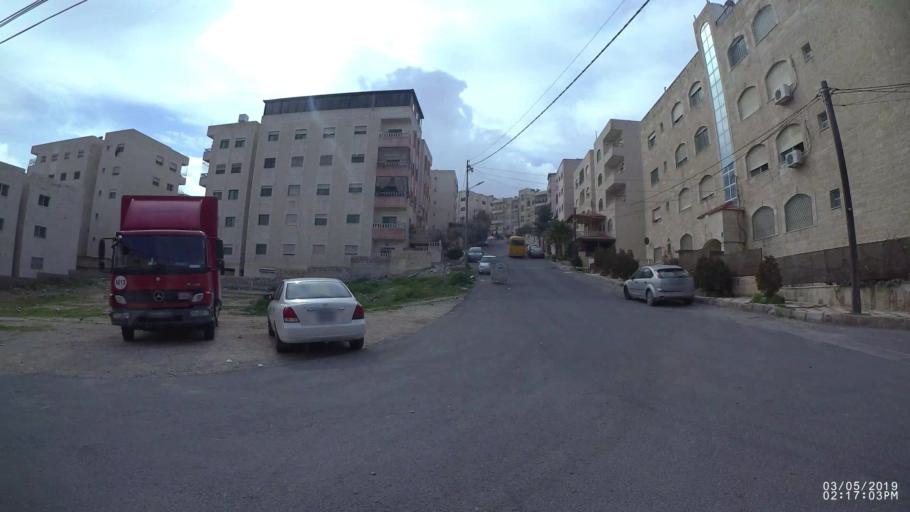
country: JO
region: Amman
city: Amman
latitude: 32.0090
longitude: 35.9379
